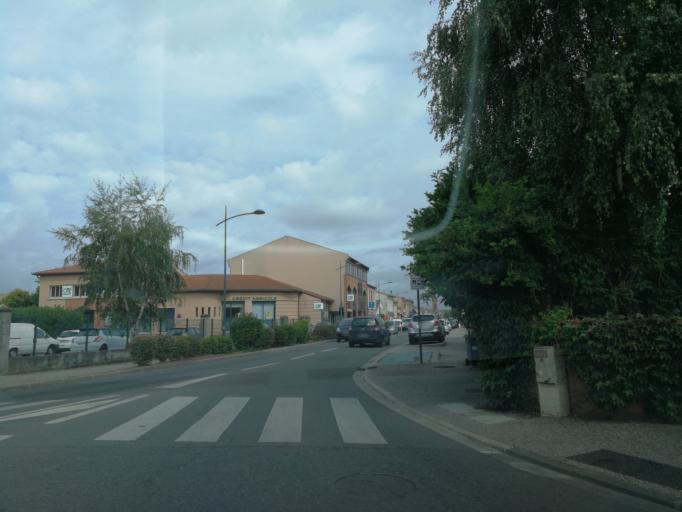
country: FR
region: Midi-Pyrenees
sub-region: Departement de la Haute-Garonne
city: Aucamville
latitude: 43.6618
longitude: 1.4314
